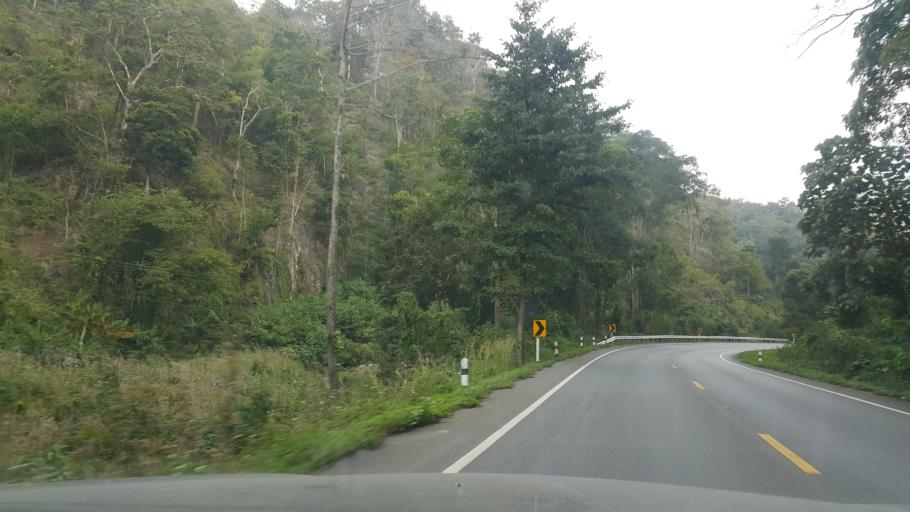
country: TH
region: Lampang
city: Wang Nuea
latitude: 19.0652
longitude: 99.7446
